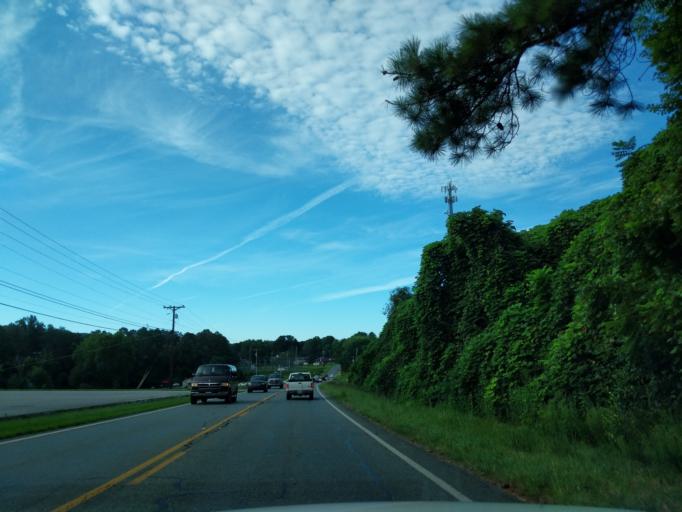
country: US
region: Georgia
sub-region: Fannin County
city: McCaysville
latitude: 34.9526
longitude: -84.3688
